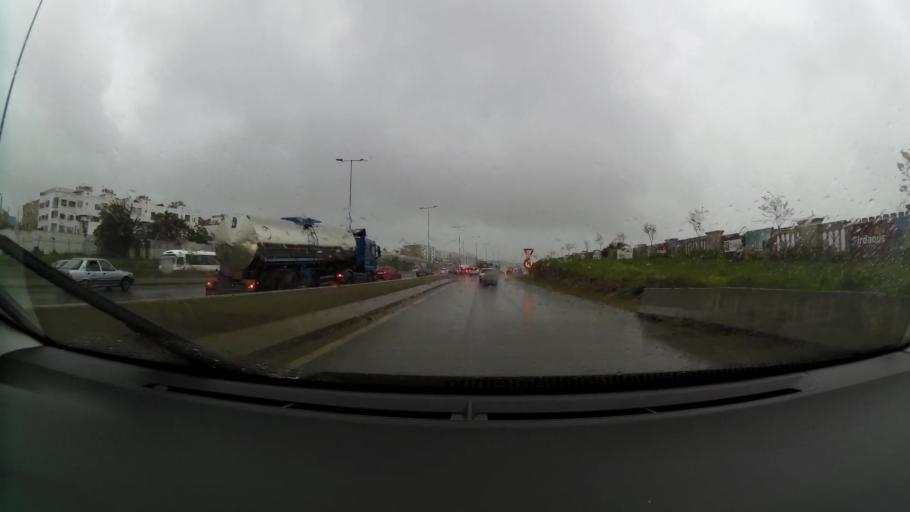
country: MA
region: Grand Casablanca
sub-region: Mediouna
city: Tit Mellil
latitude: 33.5998
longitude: -7.5102
